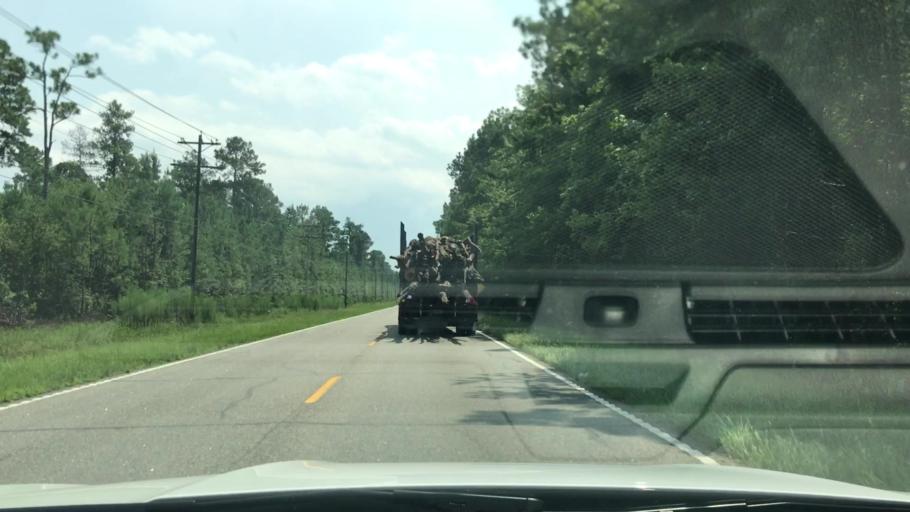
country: US
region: South Carolina
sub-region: Georgetown County
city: Georgetown
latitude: 33.4459
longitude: -79.2782
